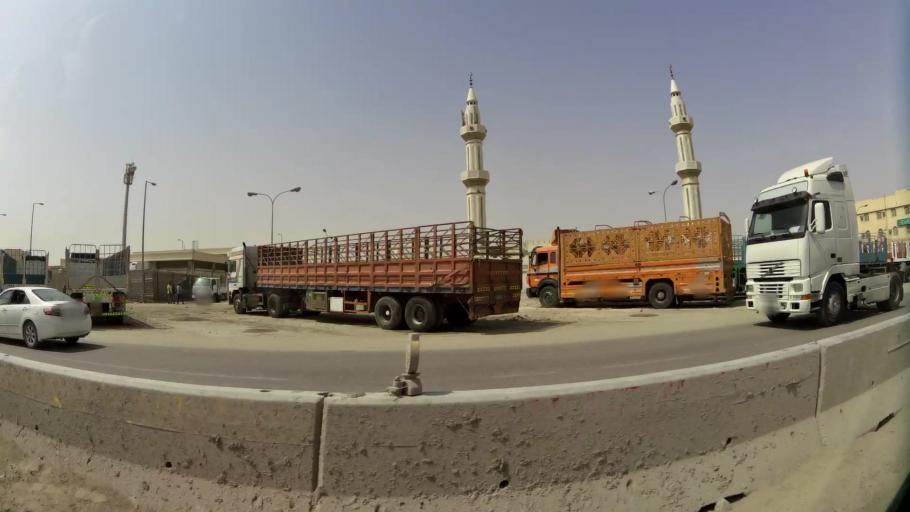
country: QA
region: Baladiyat ar Rayyan
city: Ar Rayyan
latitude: 25.1950
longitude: 51.4319
